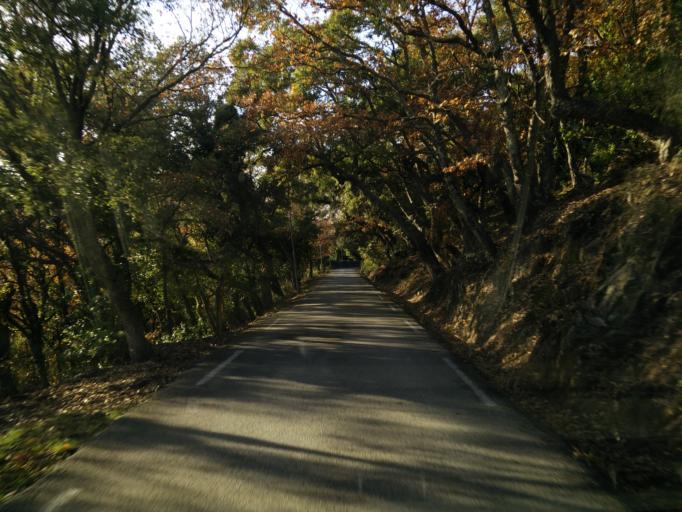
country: FR
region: Provence-Alpes-Cote d'Azur
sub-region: Departement du Var
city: La Garde-Freinet
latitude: 43.3385
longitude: 6.4799
